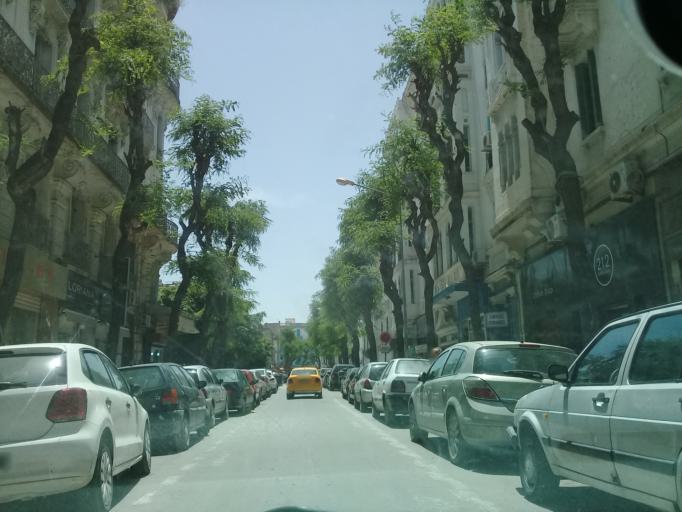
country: TN
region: Tunis
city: Tunis
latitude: 36.7962
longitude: 10.1790
